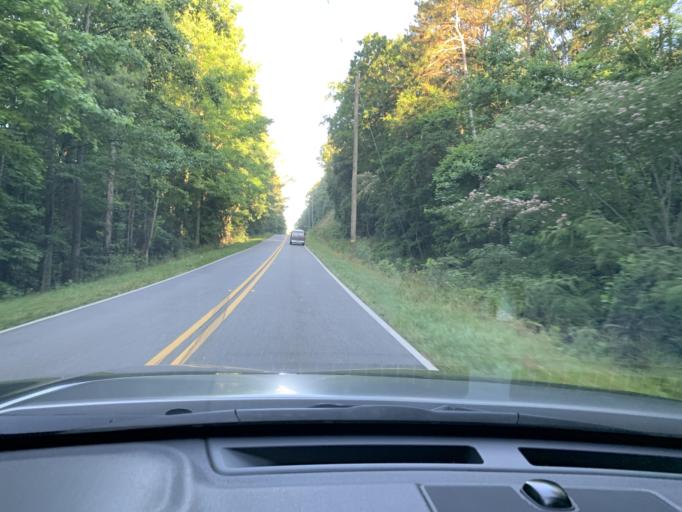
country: US
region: Georgia
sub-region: Bartow County
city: Rydal
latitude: 34.2685
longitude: -84.7162
